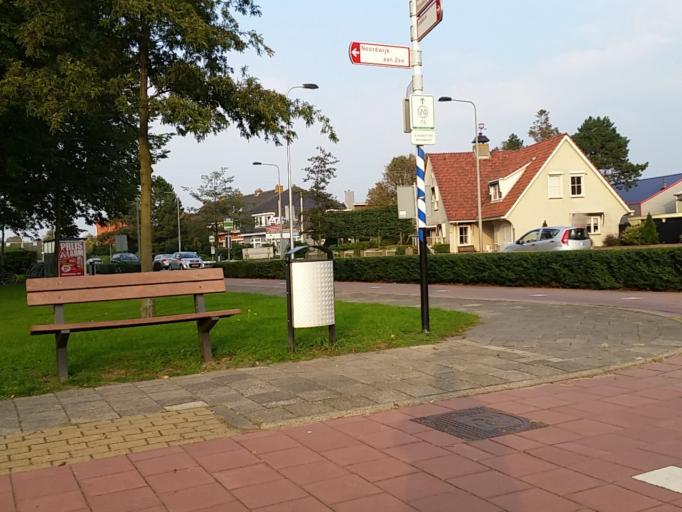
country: NL
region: South Holland
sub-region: Gemeente Noordwijk
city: Noordwijk-Binnen
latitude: 52.2281
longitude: 4.4445
